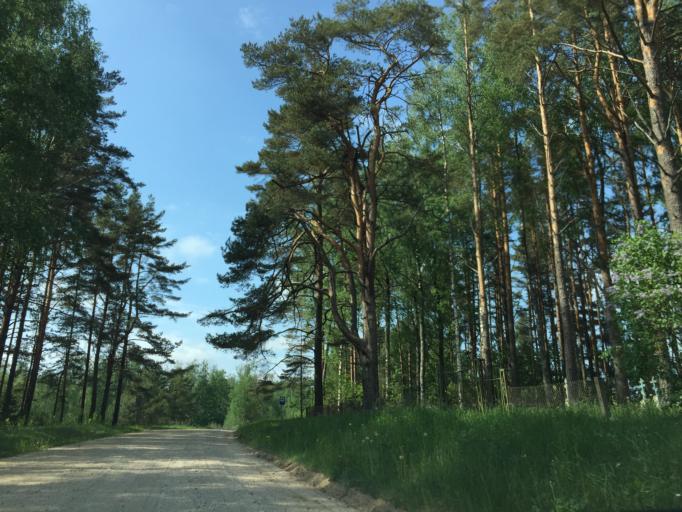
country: LV
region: Rezekne
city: Rezekne
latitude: 56.3157
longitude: 27.3992
